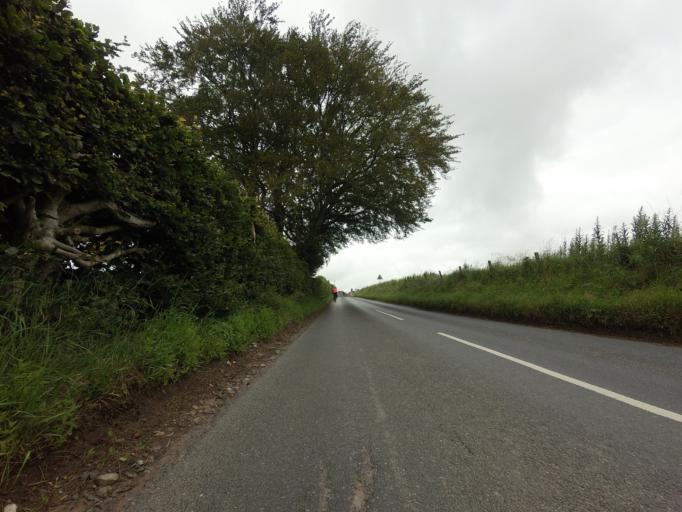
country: GB
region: Scotland
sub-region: Aberdeenshire
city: Turriff
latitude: 57.5436
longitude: -2.3387
